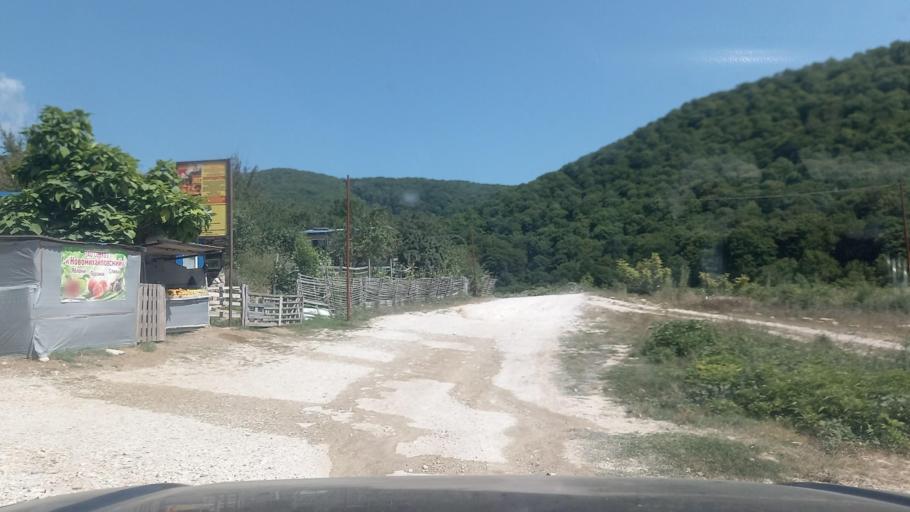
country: RU
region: Krasnodarskiy
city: Lermontovo
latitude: 44.3266
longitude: 38.7937
